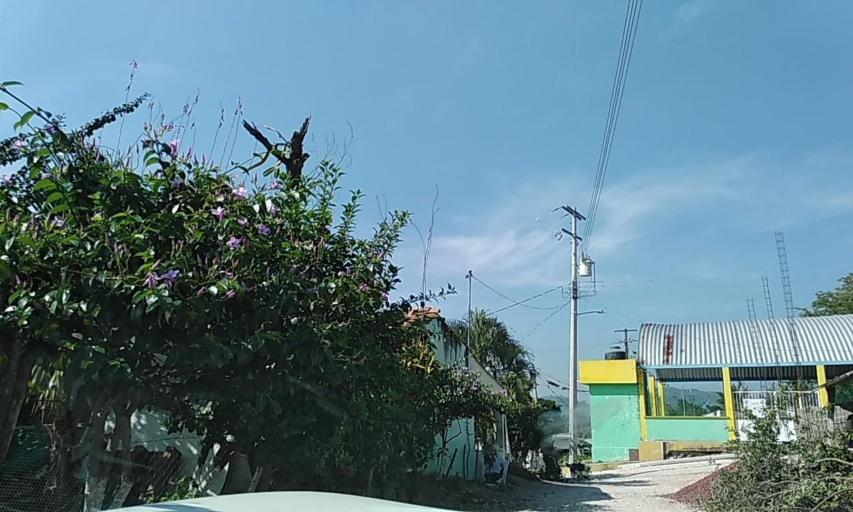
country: MX
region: Veracruz
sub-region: Emiliano Zapata
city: Plan del Rio
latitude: 19.4528
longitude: -96.6783
